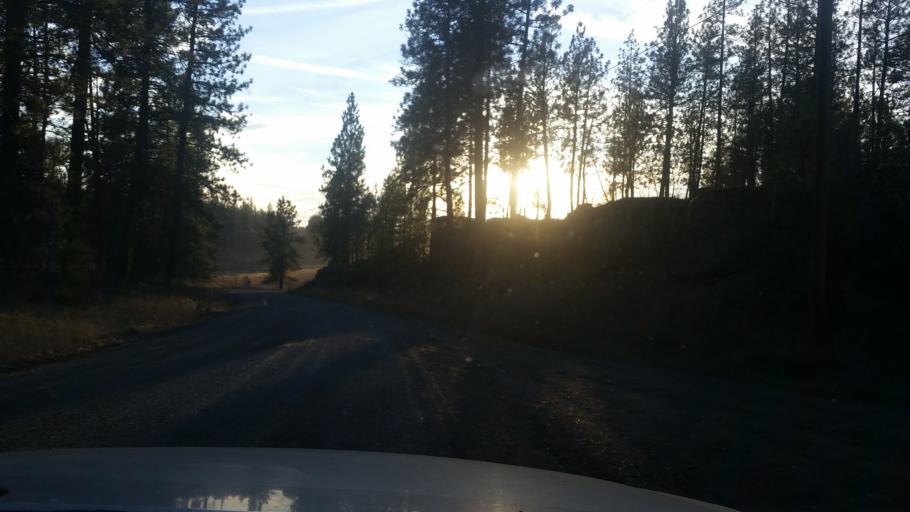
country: US
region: Washington
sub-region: Spokane County
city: Cheney
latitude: 47.5065
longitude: -117.5342
